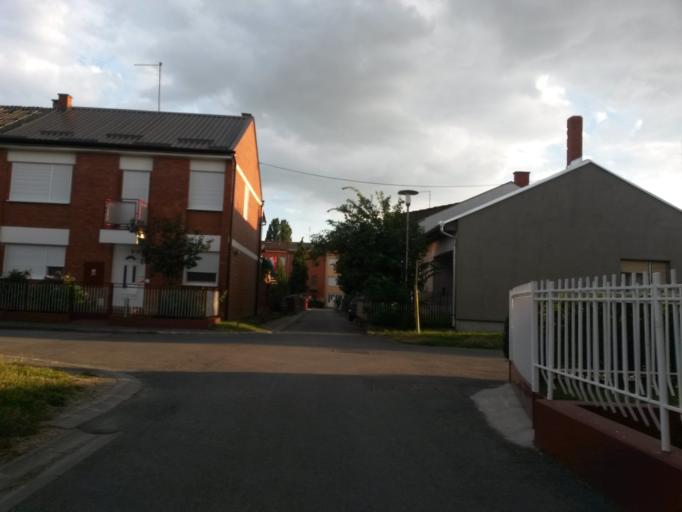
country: HR
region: Osjecko-Baranjska
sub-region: Grad Osijek
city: Osijek
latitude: 45.5468
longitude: 18.7250
